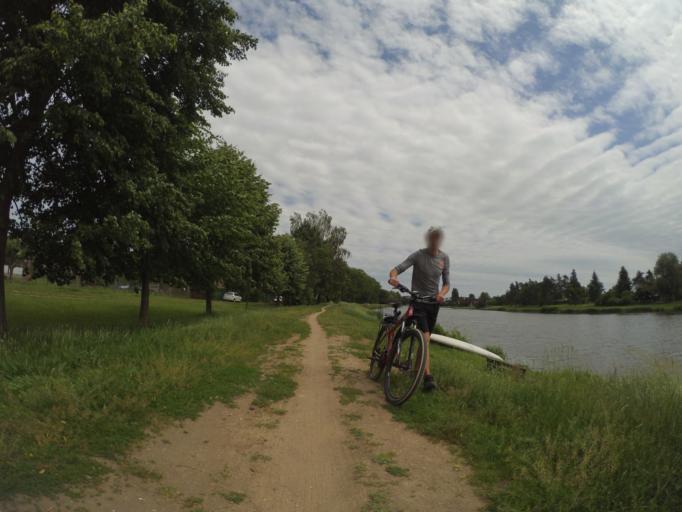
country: CZ
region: Central Bohemia
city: Celakovice
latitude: 50.1732
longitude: 14.7649
